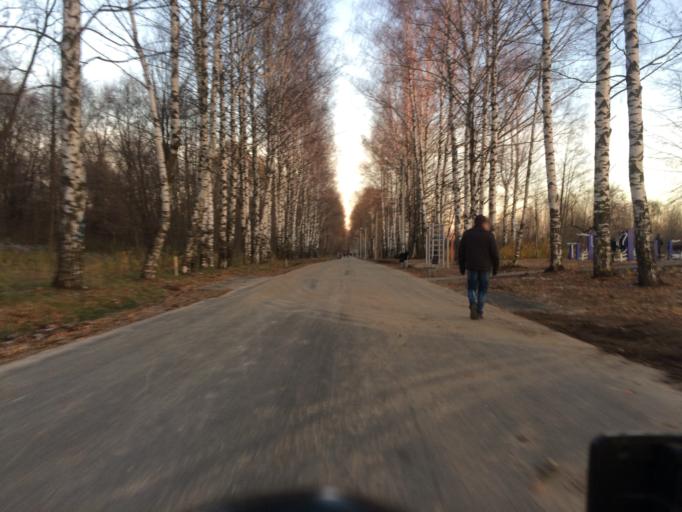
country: RU
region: Mariy-El
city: Yoshkar-Ola
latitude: 56.6253
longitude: 47.9086
